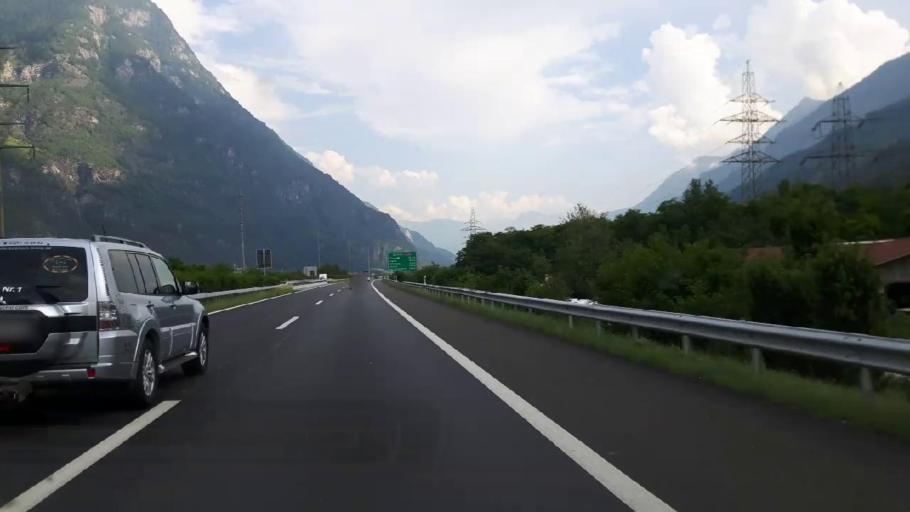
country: CH
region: Ticino
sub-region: Riviera District
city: Biasca
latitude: 46.3504
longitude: 8.9623
